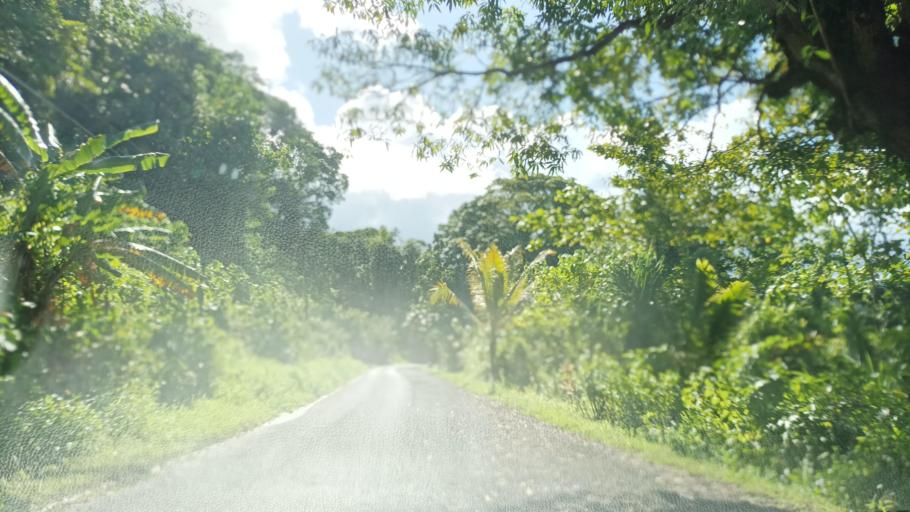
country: FM
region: Pohnpei
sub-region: Madolenihm Municipality
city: Madolenihm Municipality Government
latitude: 6.8553
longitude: 158.2956
